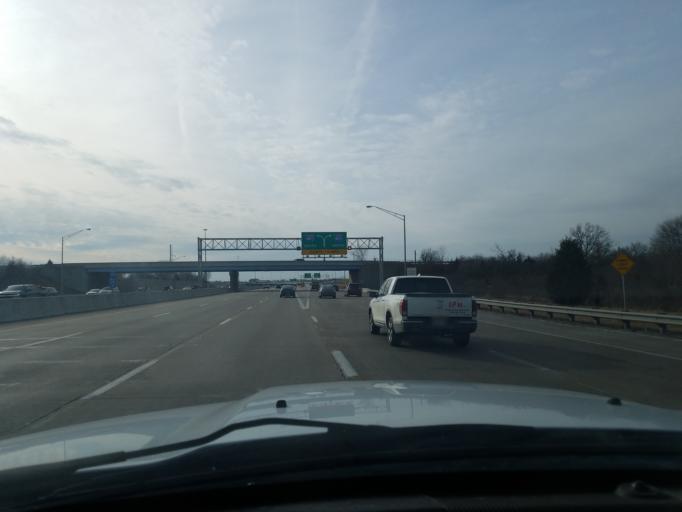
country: US
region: Indiana
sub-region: Marion County
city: Warren Park
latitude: 39.7998
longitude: -86.0240
